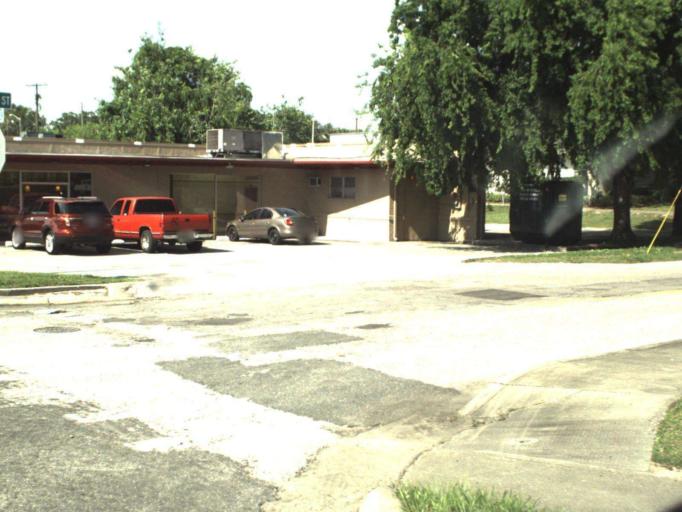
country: US
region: Florida
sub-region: Marion County
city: Ocala
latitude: 29.1776
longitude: -82.1404
